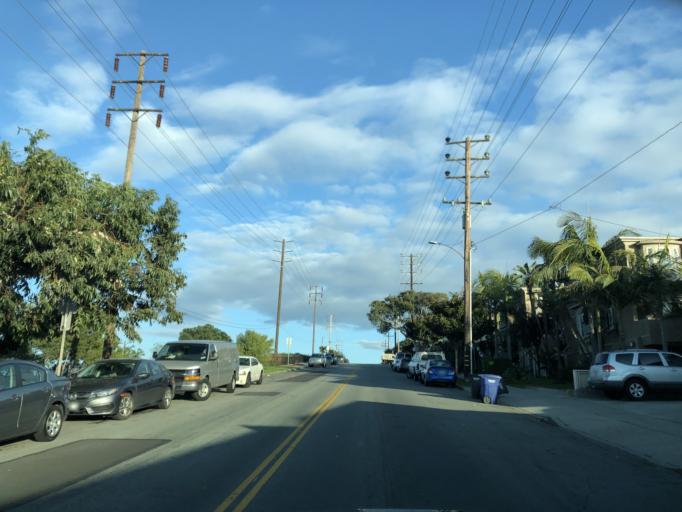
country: US
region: California
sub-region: Los Angeles County
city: El Segundo
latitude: 33.9309
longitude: -118.4134
